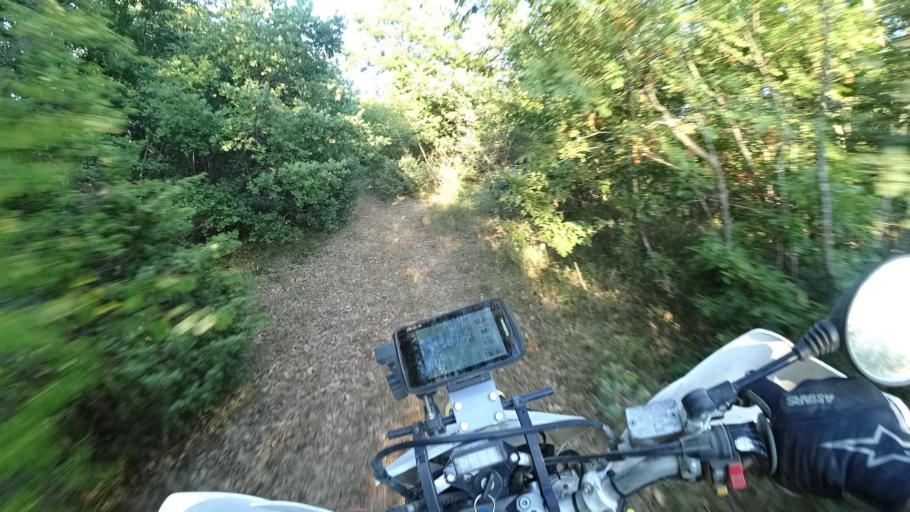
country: HR
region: Istarska
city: Marcana
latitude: 44.9603
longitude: 13.9220
